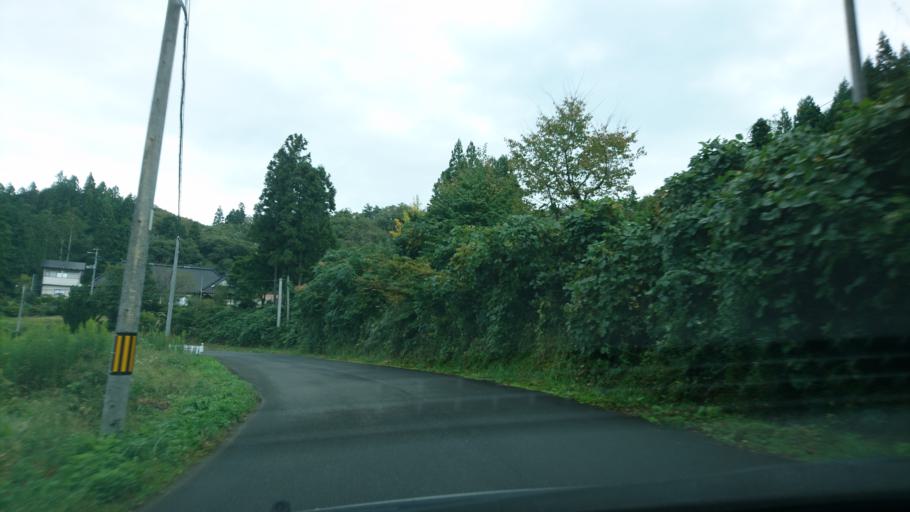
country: JP
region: Iwate
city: Ichinoseki
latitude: 38.9061
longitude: 141.0820
